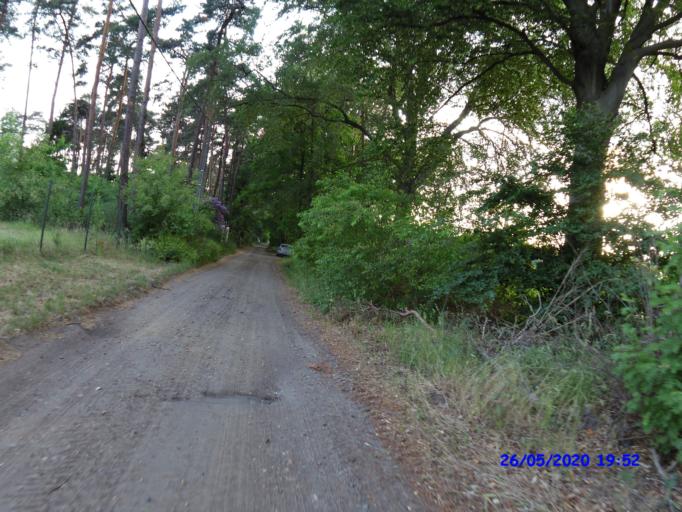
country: BE
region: Flanders
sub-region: Provincie Antwerpen
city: Vorselaar
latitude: 51.1694
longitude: 4.7844
